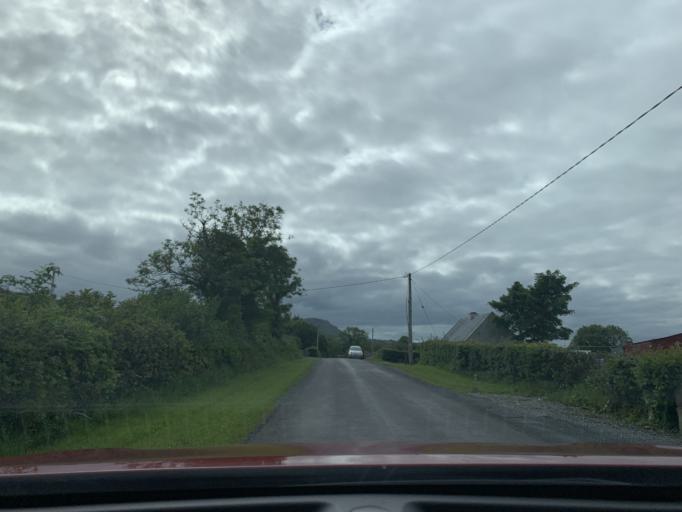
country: IE
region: Connaught
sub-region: Sligo
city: Sligo
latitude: 54.3390
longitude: -8.4780
